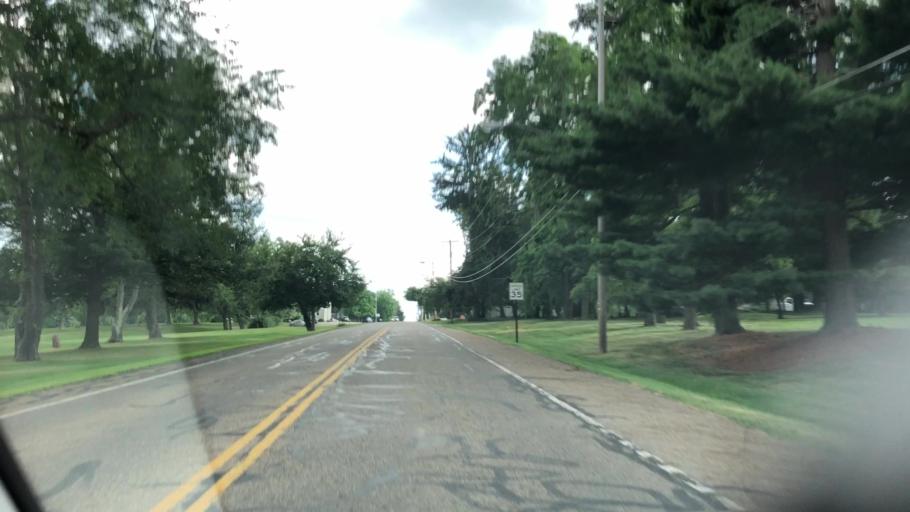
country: US
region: Ohio
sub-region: Summit County
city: Norton
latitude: 41.0617
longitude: -81.6376
